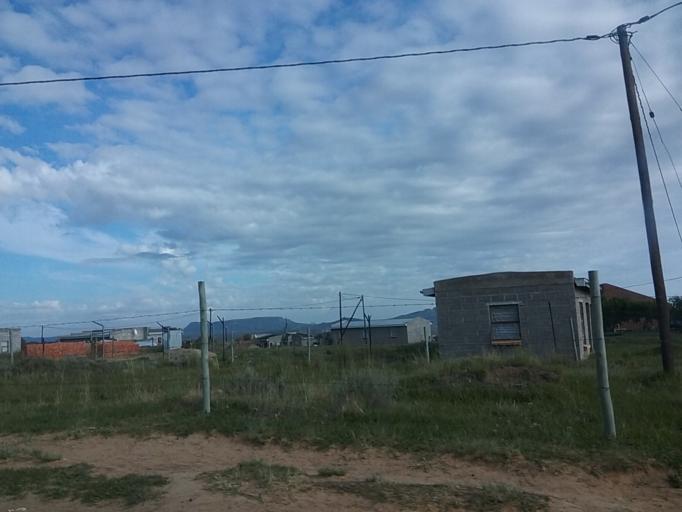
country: LS
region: Berea
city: Teyateyaneng
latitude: -29.1303
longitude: 27.7598
